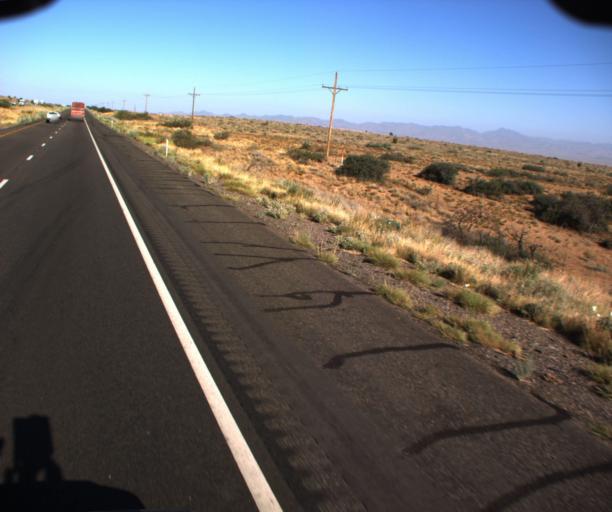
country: US
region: Arizona
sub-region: Mohave County
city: New Kingman-Butler
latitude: 35.1956
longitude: -113.8601
